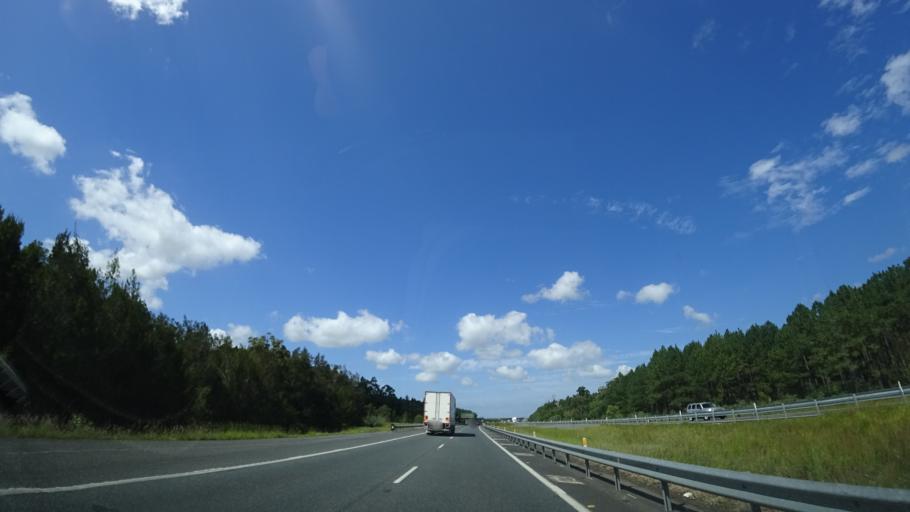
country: AU
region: Queensland
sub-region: Sunshine Coast
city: Little Mountain
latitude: -26.8630
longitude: 153.0151
